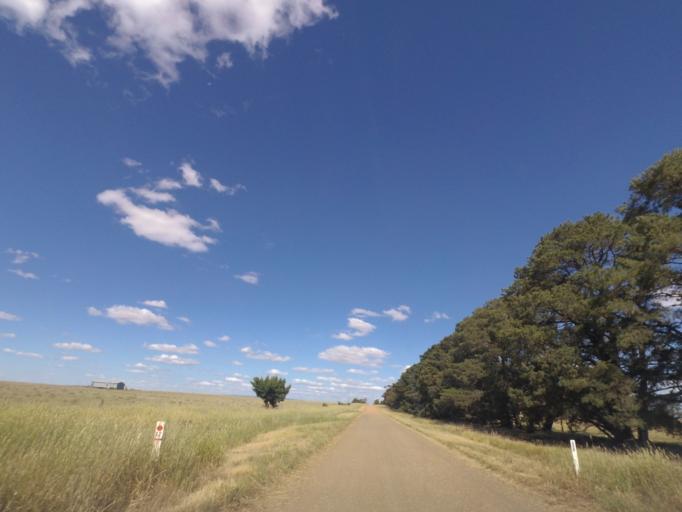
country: AU
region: Victoria
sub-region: Hume
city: Sunbury
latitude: -37.4600
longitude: 144.8011
